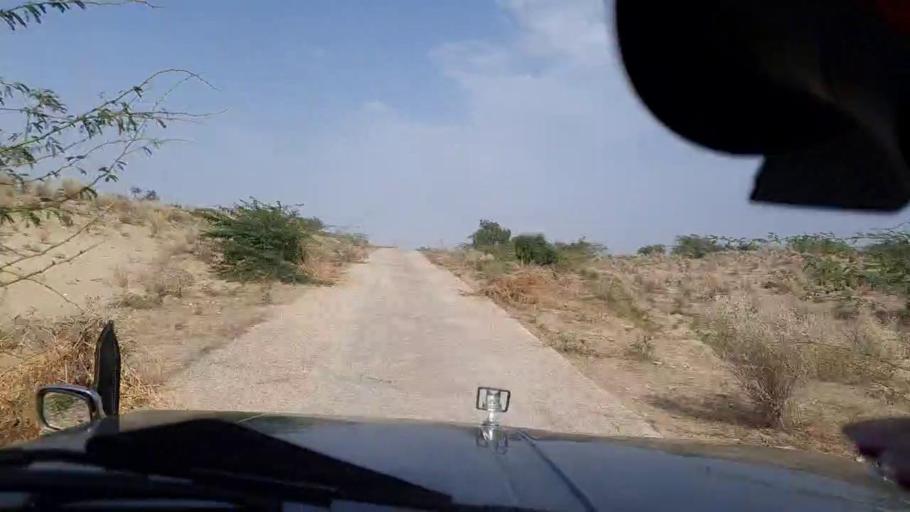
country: PK
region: Sindh
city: Diplo
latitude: 24.4291
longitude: 69.4220
